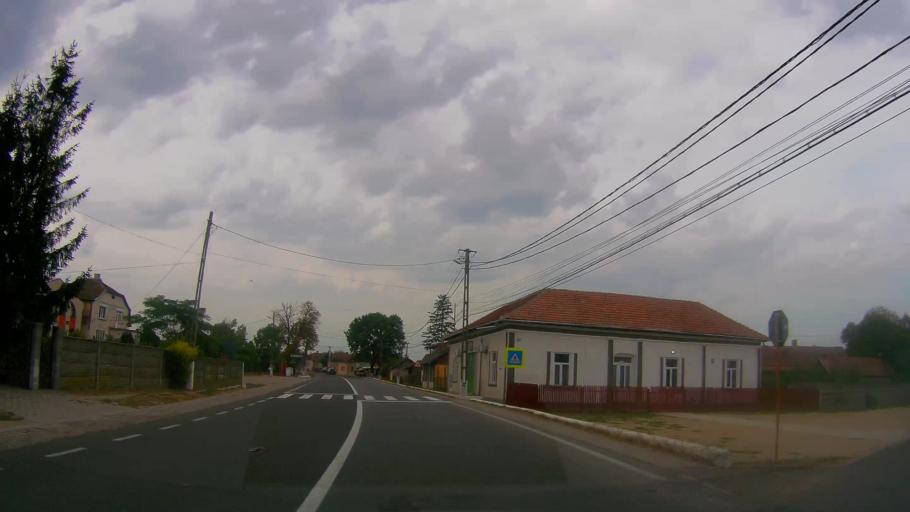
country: RO
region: Satu Mare
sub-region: Comuna Acas
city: Acas
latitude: 47.5395
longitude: 22.7844
